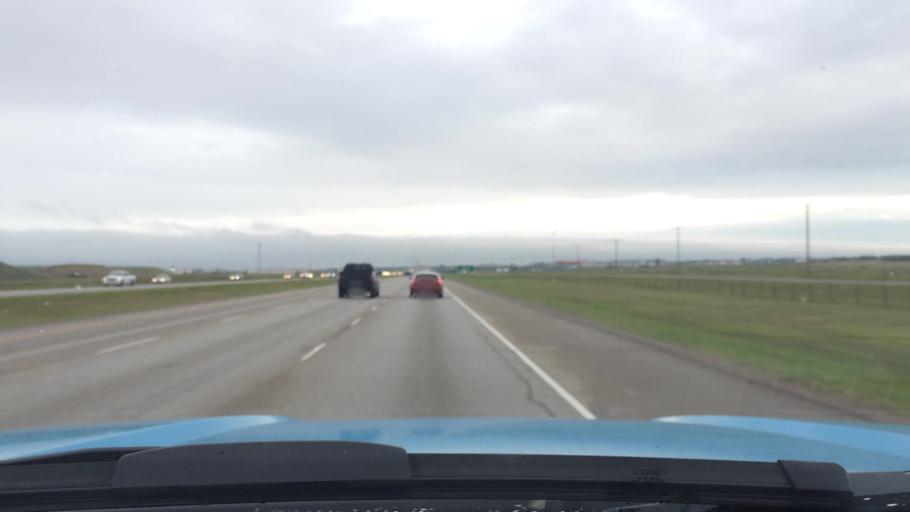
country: CA
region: Alberta
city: Airdrie
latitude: 51.2470
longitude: -114.0012
